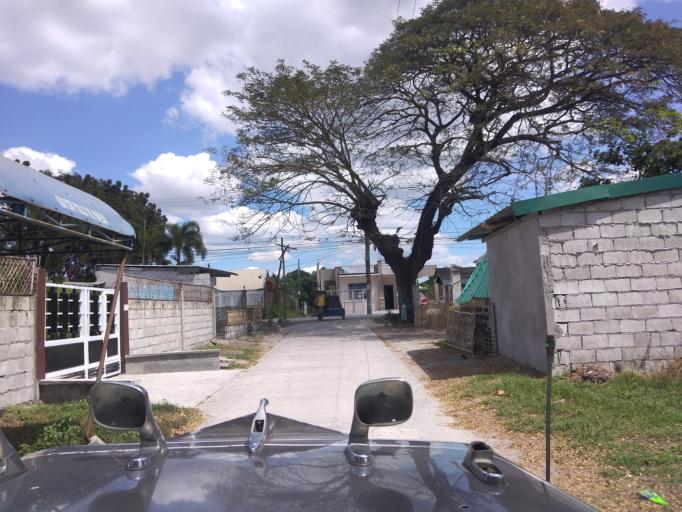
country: PH
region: Central Luzon
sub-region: Province of Pampanga
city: Santa Rita
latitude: 15.0093
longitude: 120.5948
